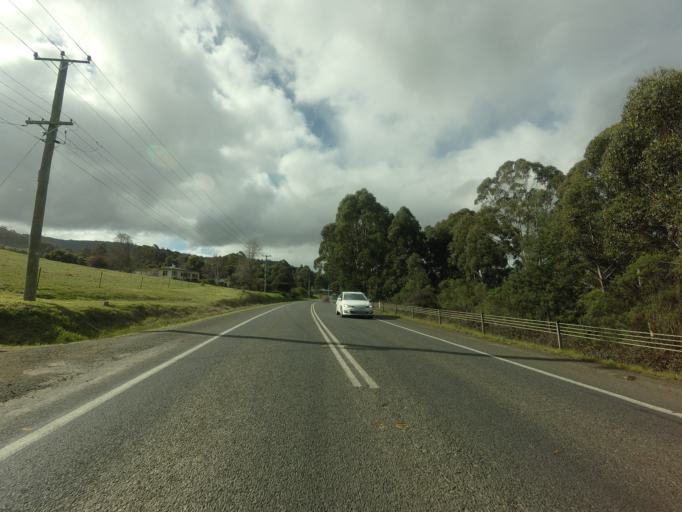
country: AU
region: Tasmania
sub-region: Huon Valley
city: Franklin
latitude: -43.0645
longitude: 147.0254
